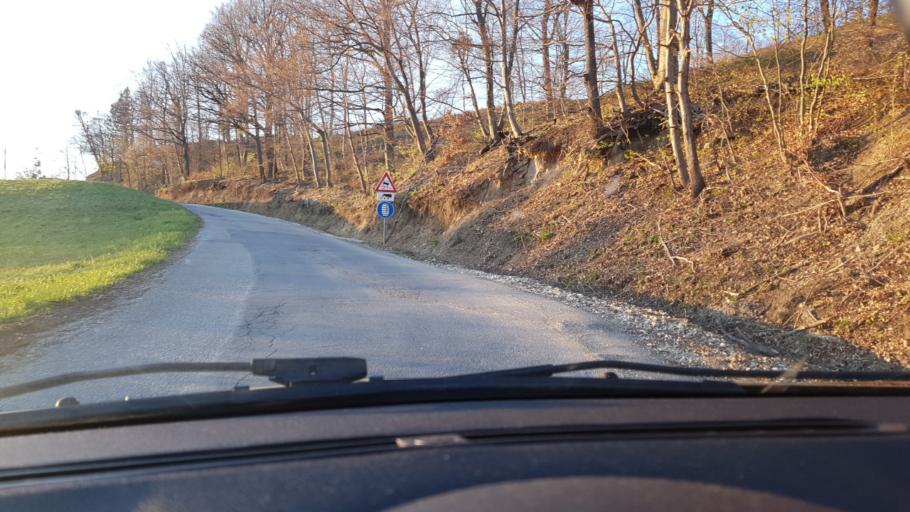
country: SI
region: Rogatec
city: Rogatec
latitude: 46.1759
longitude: 15.6838
